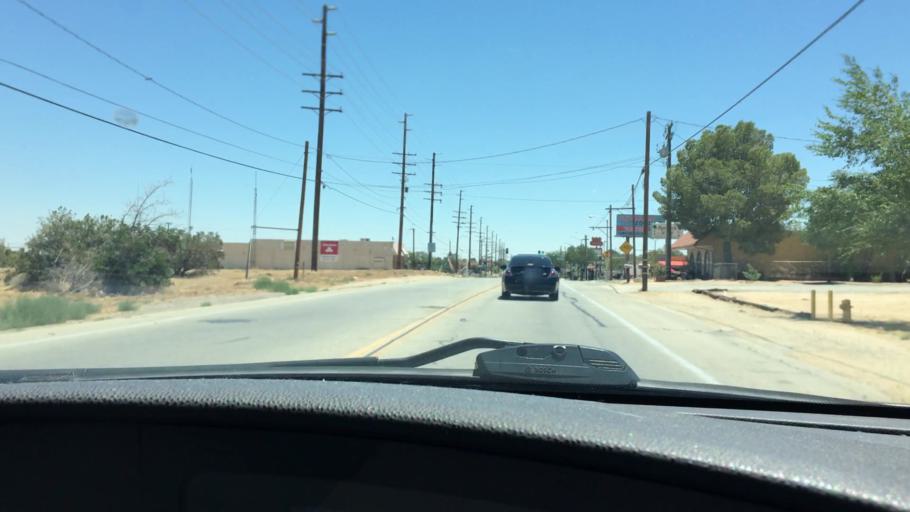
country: US
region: California
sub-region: Los Angeles County
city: Quartz Hill
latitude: 34.6602
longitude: -118.2124
